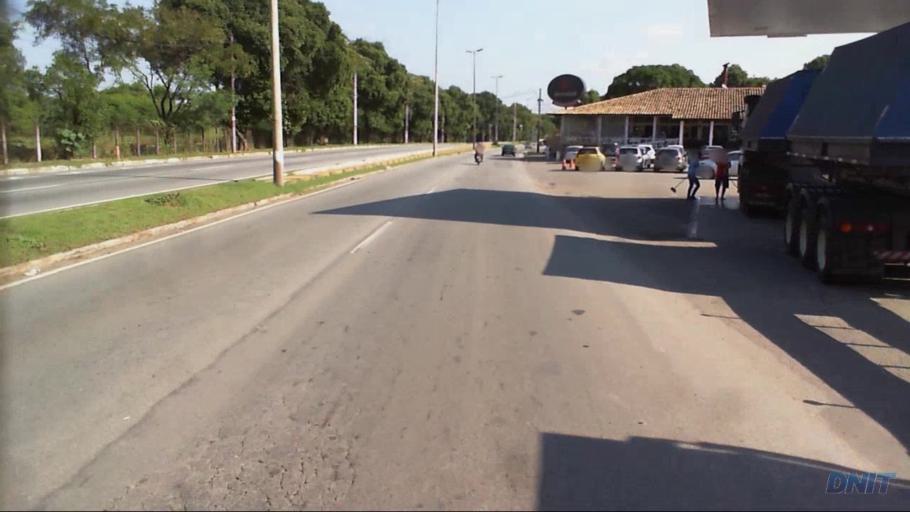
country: BR
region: Minas Gerais
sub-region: Ipatinga
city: Ipatinga
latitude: -19.5030
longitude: -42.5677
